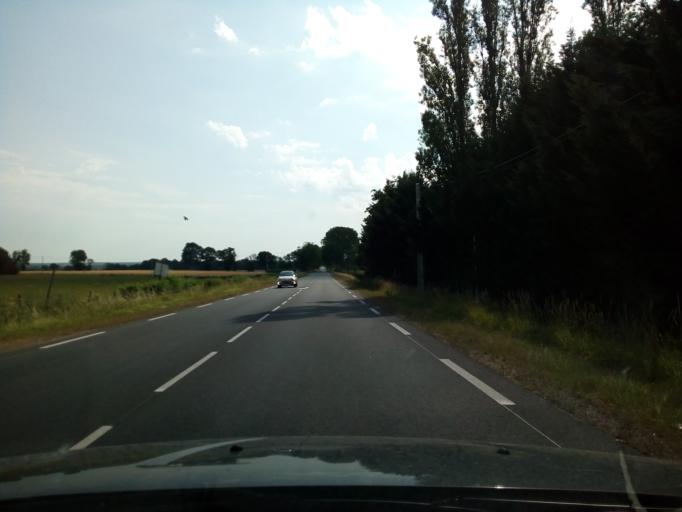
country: FR
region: Auvergne
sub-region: Departement de l'Allier
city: Saint-Pourcain-sur-Sioule
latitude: 46.3163
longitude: 3.3252
